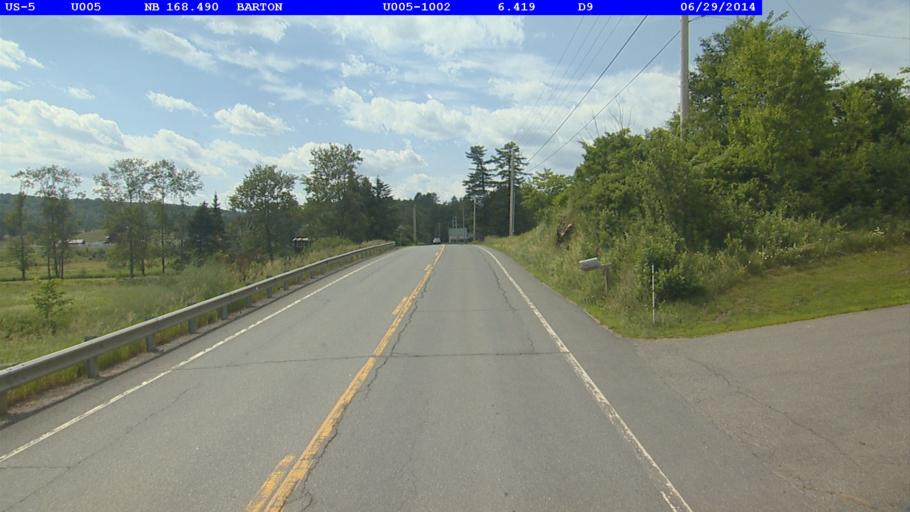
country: US
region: Vermont
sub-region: Orleans County
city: Newport
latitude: 44.7579
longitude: -72.1908
